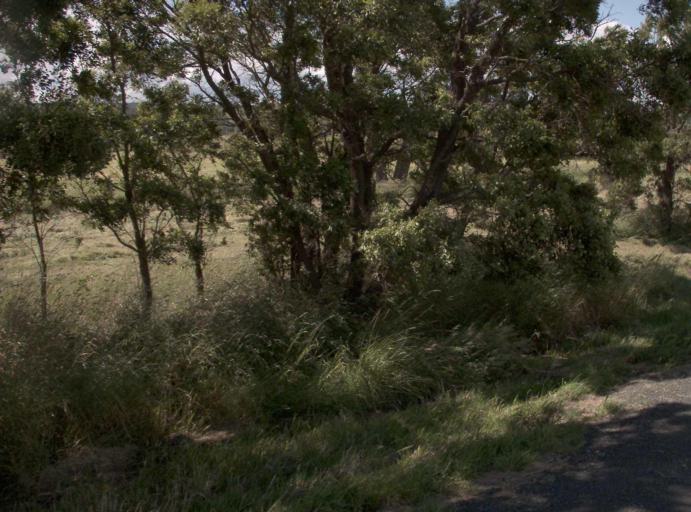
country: AU
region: Victoria
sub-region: Latrobe
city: Traralgon
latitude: -38.1448
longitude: 146.5254
